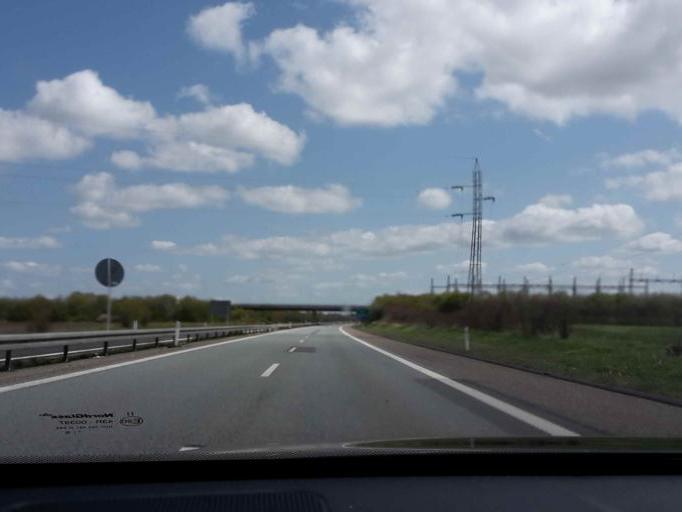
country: DK
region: South Denmark
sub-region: Vejen Kommune
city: Holsted
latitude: 55.5213
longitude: 8.9131
